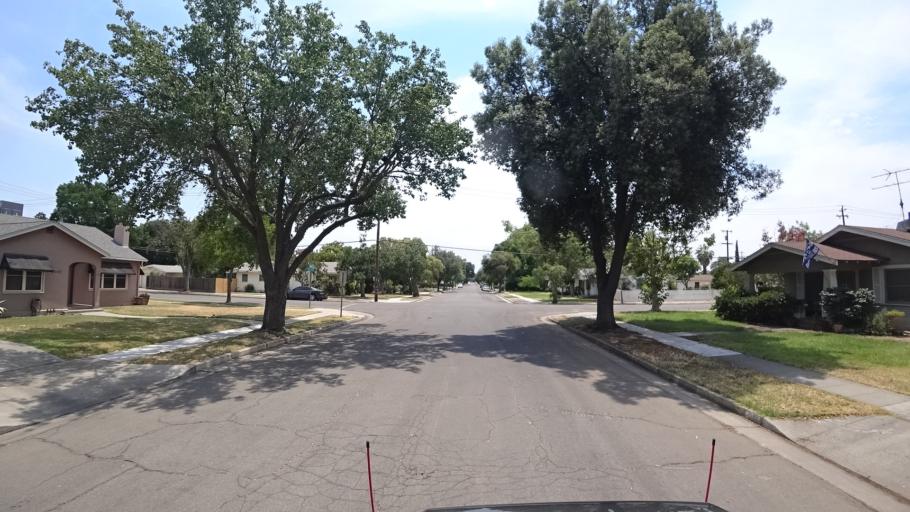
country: US
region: California
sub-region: Fresno County
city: Fresno
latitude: 36.7688
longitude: -119.8165
